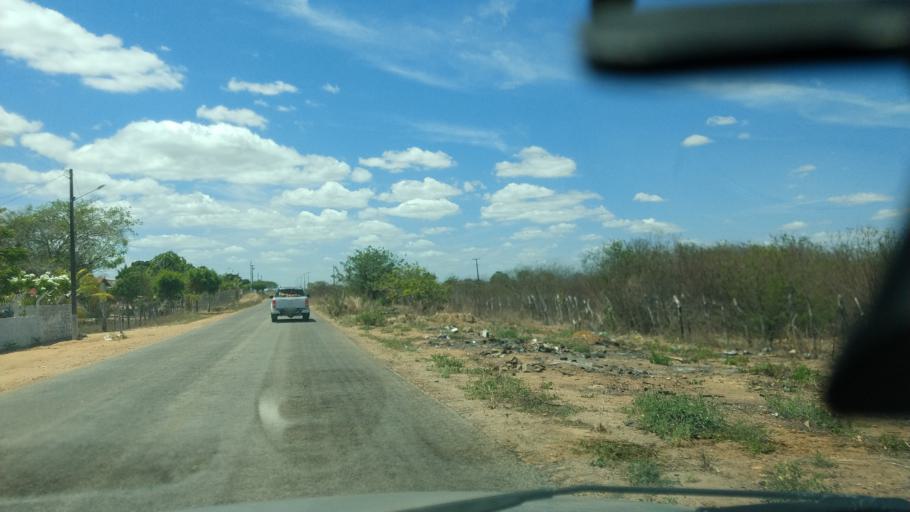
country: BR
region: Rio Grande do Norte
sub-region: Sao Paulo Do Potengi
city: Sao Paulo do Potengi
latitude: -5.9150
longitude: -35.7368
